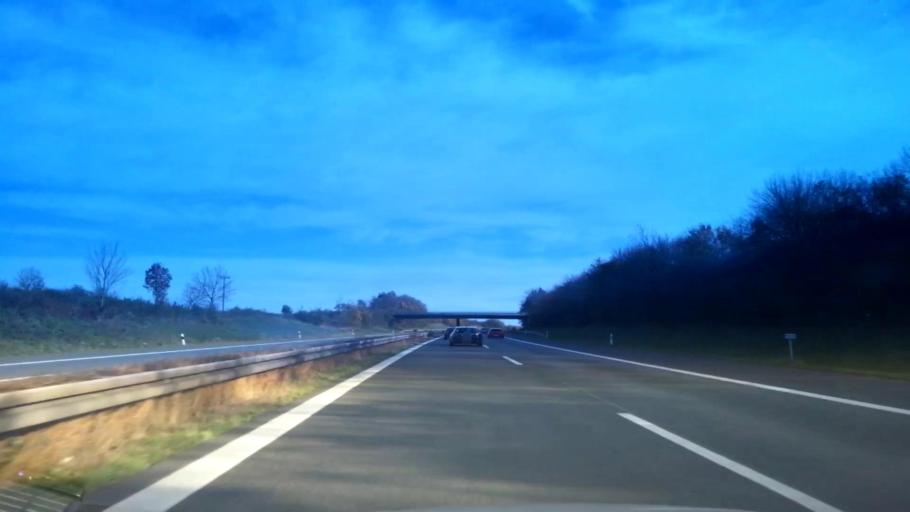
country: DE
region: Bavaria
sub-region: Upper Franconia
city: Schesslitz
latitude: 49.9759
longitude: 11.0191
